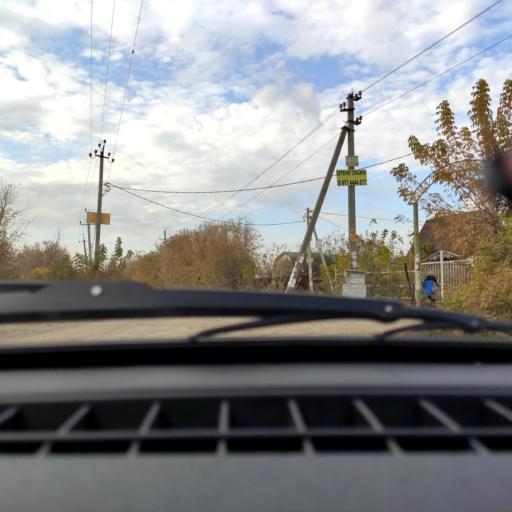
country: RU
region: Bashkortostan
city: Ufa
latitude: 54.7703
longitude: 55.9370
